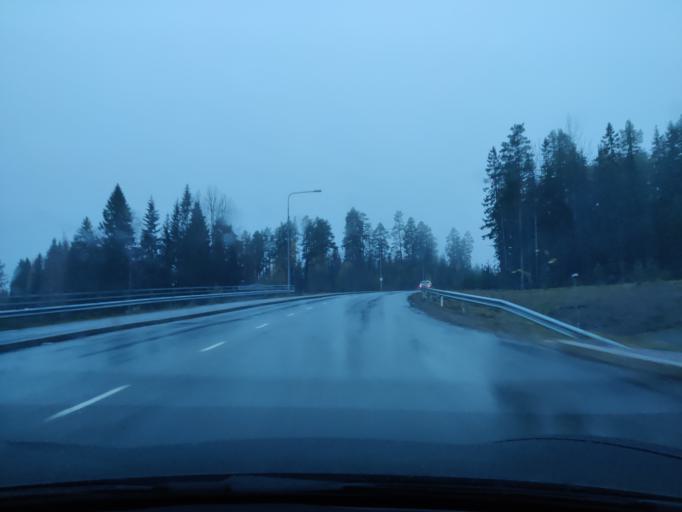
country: FI
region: Northern Savo
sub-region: Kuopio
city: Kuopio
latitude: 62.8325
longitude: 27.7117
